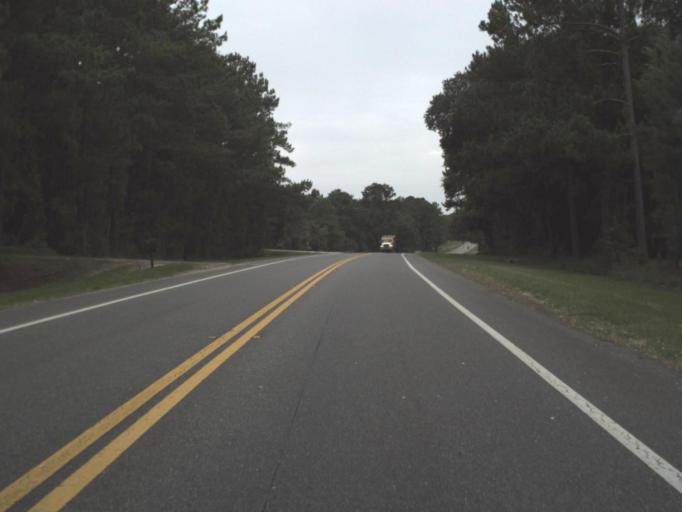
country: US
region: Florida
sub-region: Suwannee County
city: Live Oak
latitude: 30.1588
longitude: -82.9590
